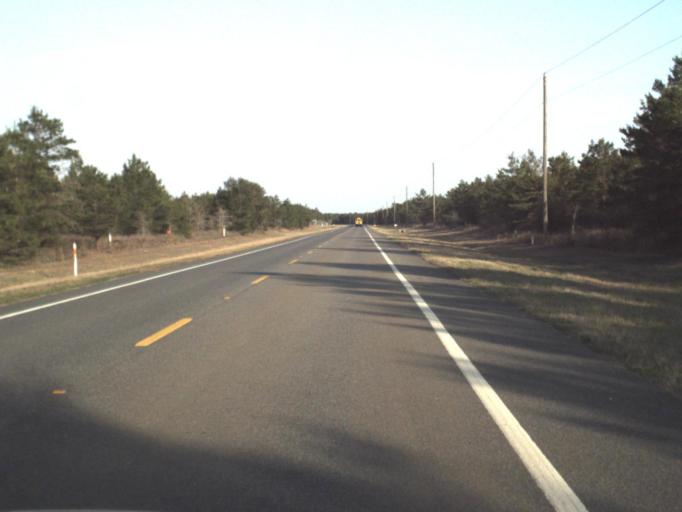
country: US
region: Florida
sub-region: Bay County
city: Lynn Haven
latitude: 30.4257
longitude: -85.6642
